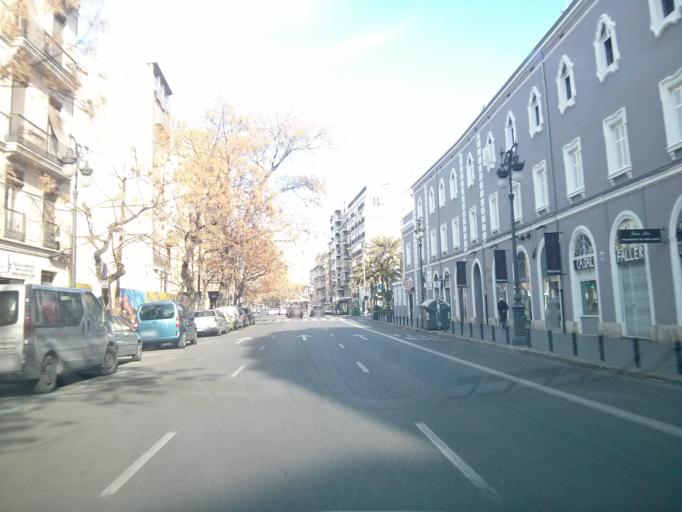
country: ES
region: Valencia
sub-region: Provincia de Valencia
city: Valencia
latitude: 39.4729
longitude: -0.3839
